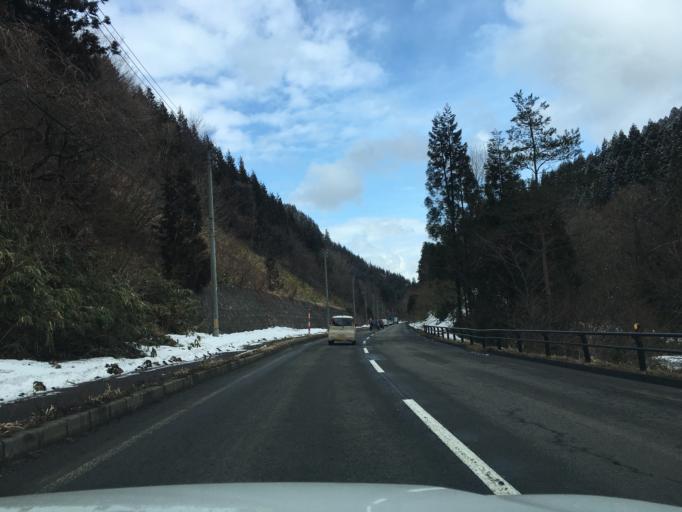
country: JP
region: Akita
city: Takanosu
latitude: 39.9935
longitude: 140.2498
